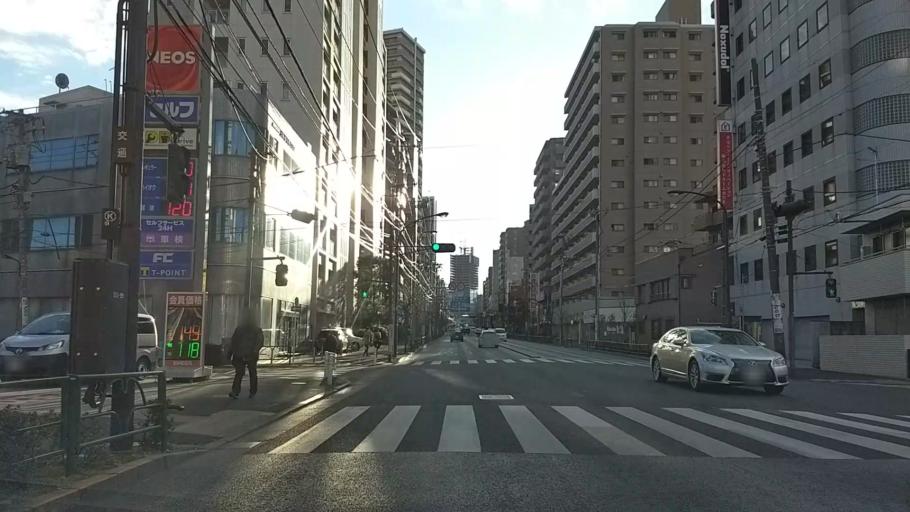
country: JP
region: Tokyo
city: Tokyo
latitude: 35.7403
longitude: 139.7243
